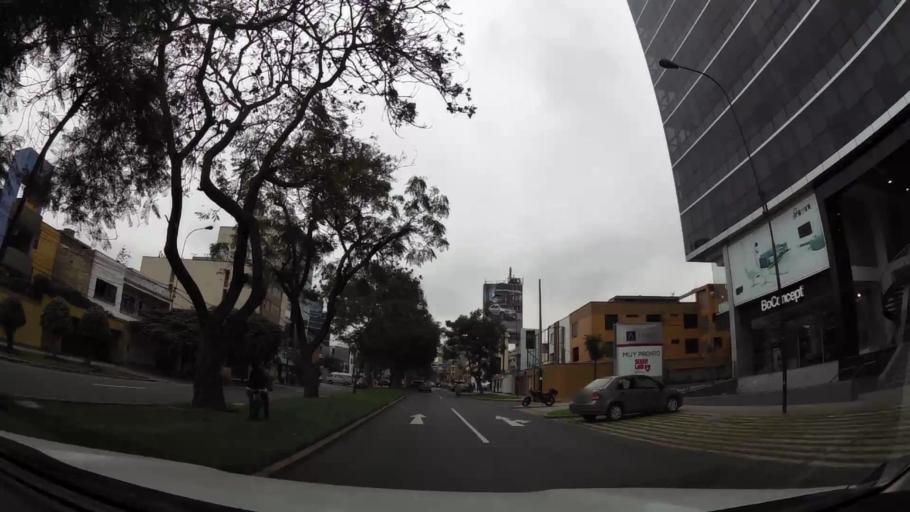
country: PE
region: Lima
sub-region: Lima
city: La Molina
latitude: -12.1059
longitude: -76.9711
